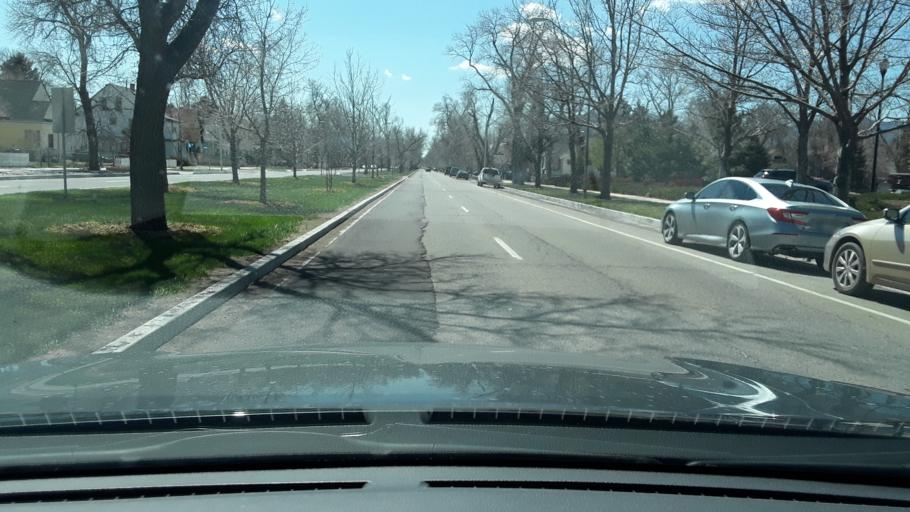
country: US
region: Colorado
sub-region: El Paso County
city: Colorado Springs
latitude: 38.8652
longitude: -104.8201
